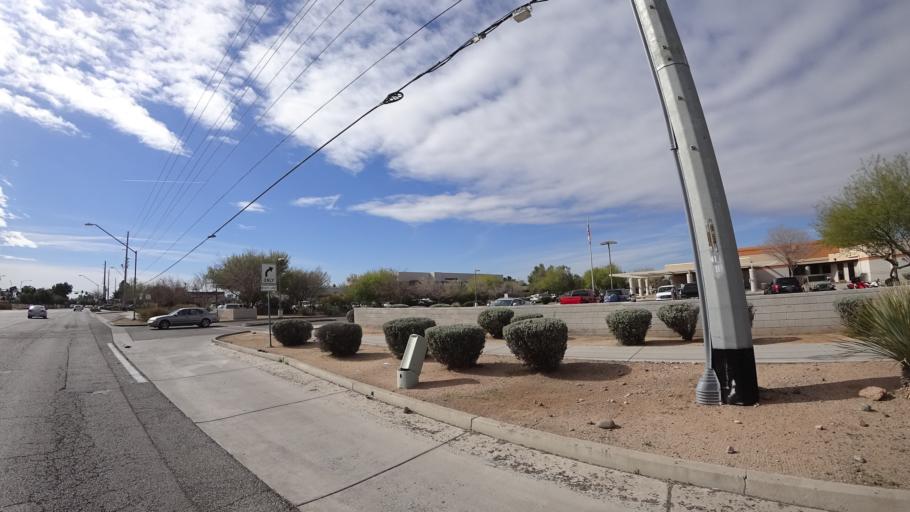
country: US
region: Arizona
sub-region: Maricopa County
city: Peoria
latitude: 33.6338
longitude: -112.1859
